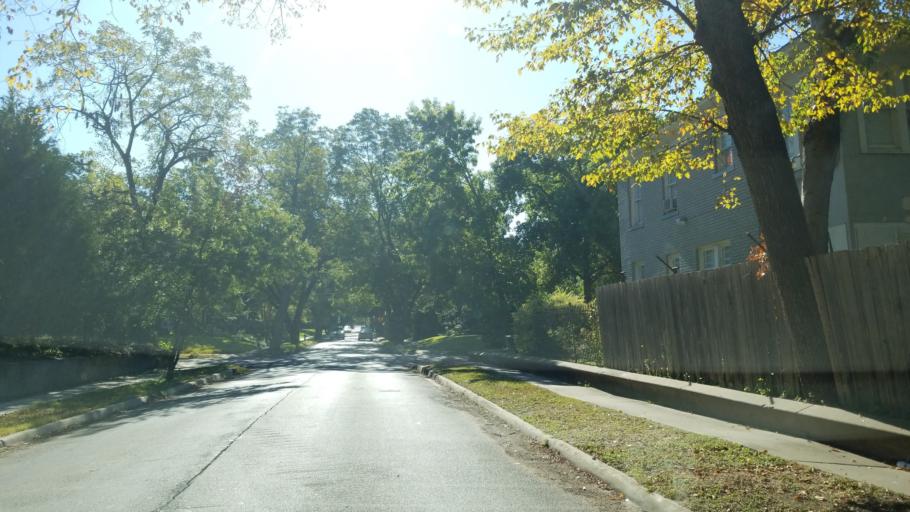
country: US
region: Texas
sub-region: Dallas County
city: Highland Park
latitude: 32.8113
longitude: -96.7615
